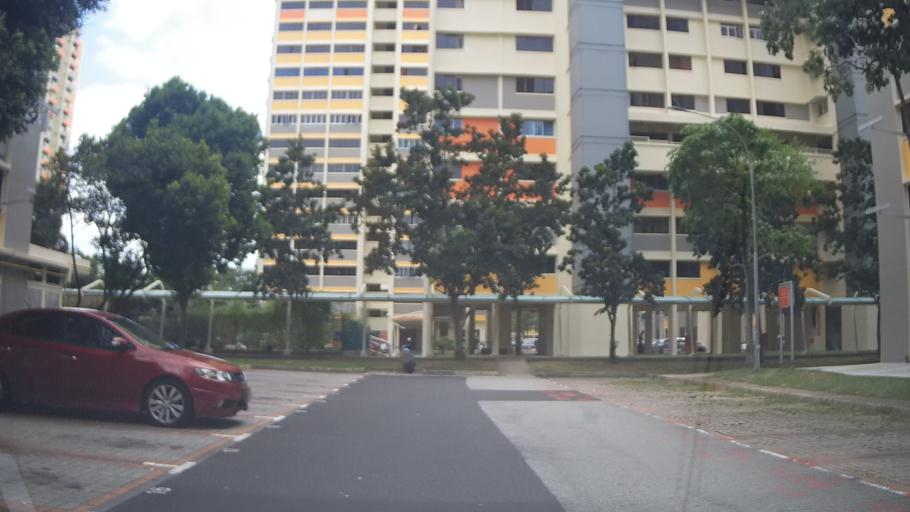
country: SG
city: Singapore
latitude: 1.3040
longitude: 103.7621
